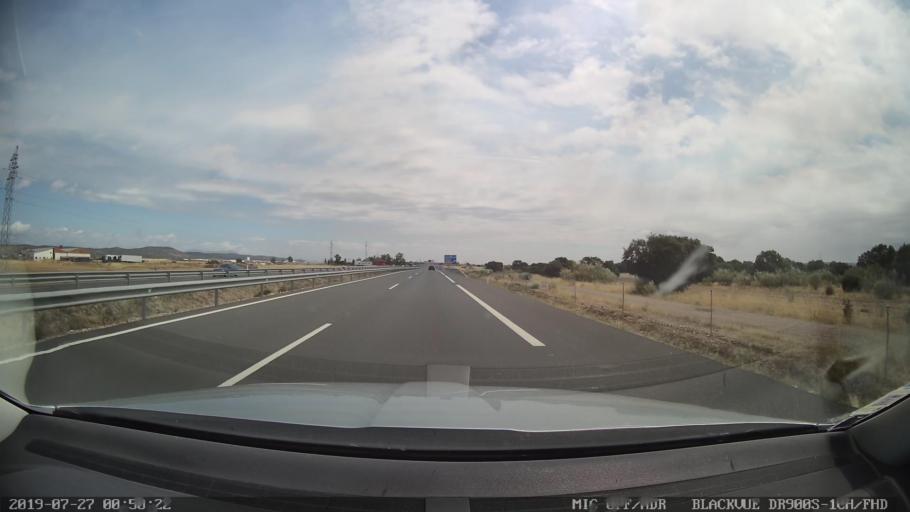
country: ES
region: Castille-La Mancha
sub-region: Province of Toledo
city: Velada
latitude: 39.9391
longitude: -4.9622
